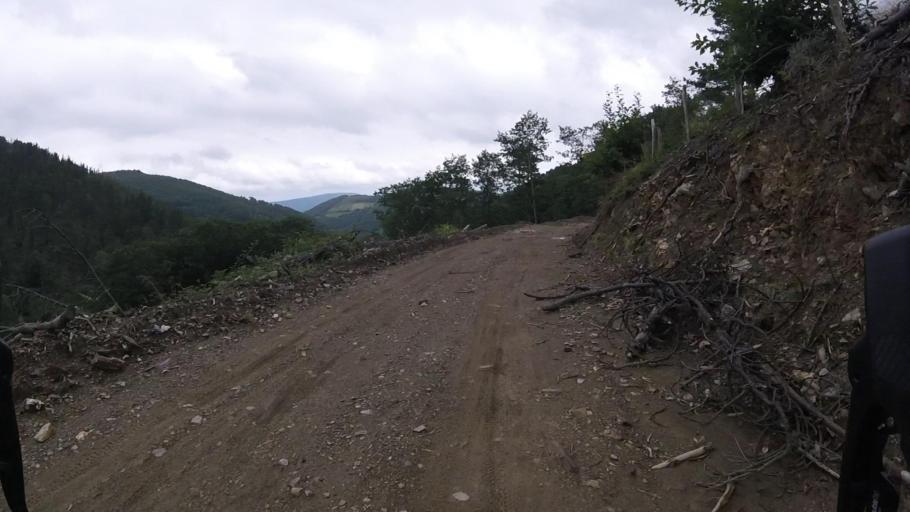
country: ES
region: Navarre
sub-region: Provincia de Navarra
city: Arano
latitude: 43.2528
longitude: -1.8584
